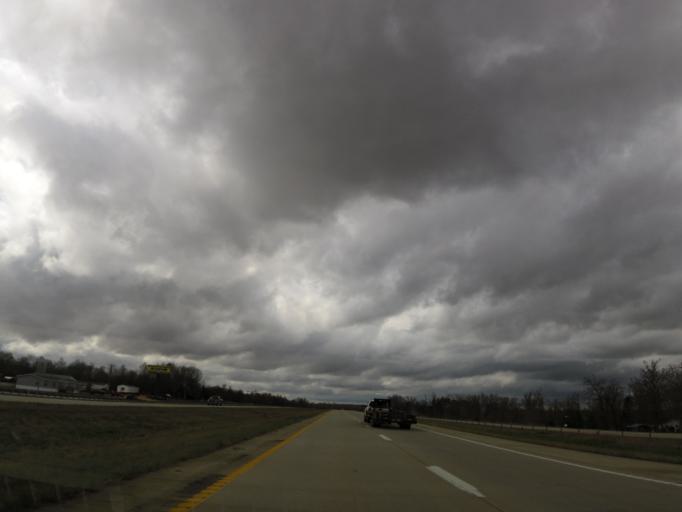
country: US
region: Missouri
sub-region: Butler County
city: Poplar Bluff
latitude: 36.7056
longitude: -90.4715
